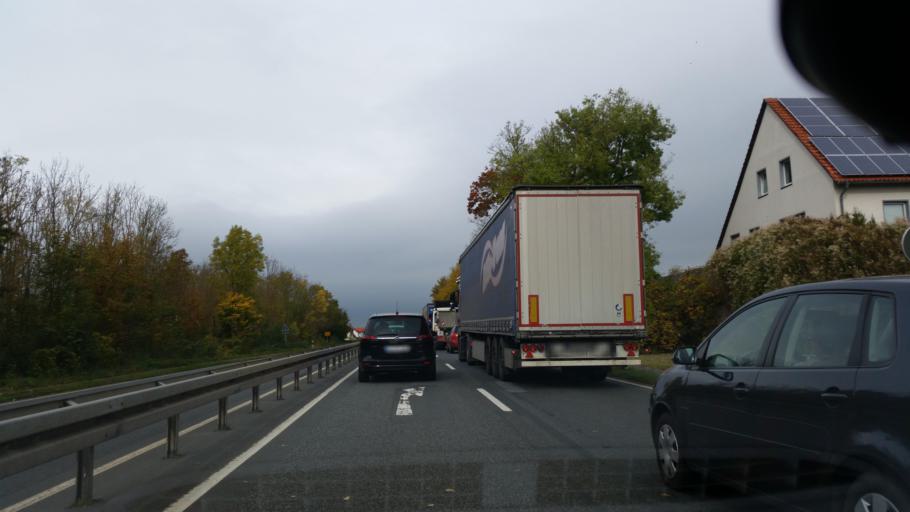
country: DE
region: Lower Saxony
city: Giesen
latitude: 52.1904
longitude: 9.9238
